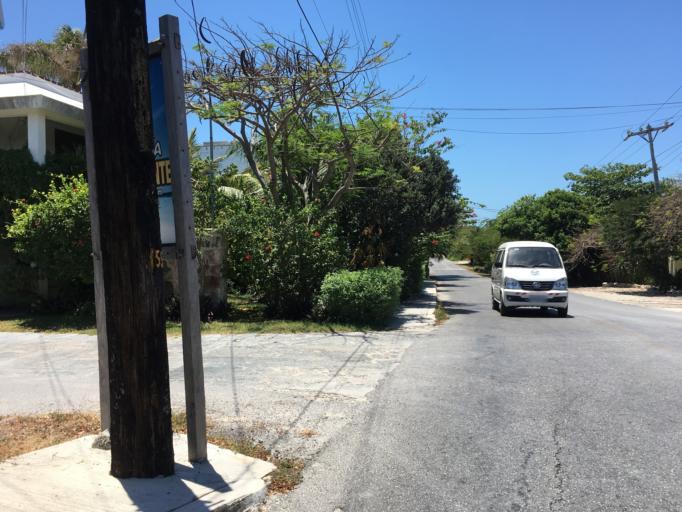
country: MX
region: Quintana Roo
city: Isla Mujeres
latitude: 21.2093
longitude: -86.7195
